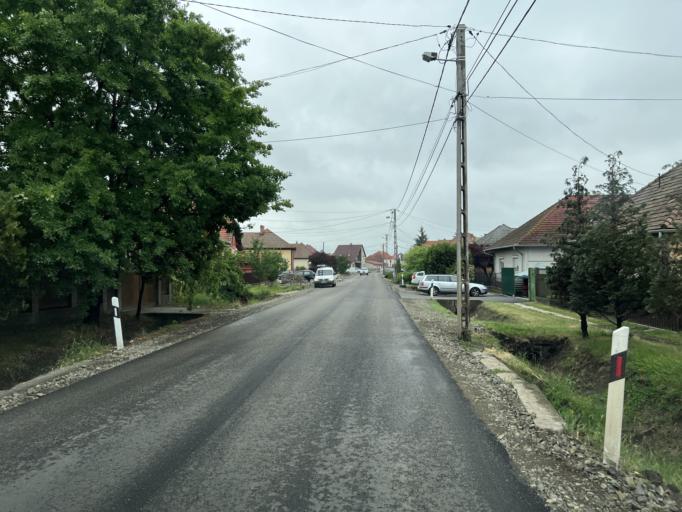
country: HU
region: Pest
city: Tura
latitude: 47.6125
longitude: 19.5861
